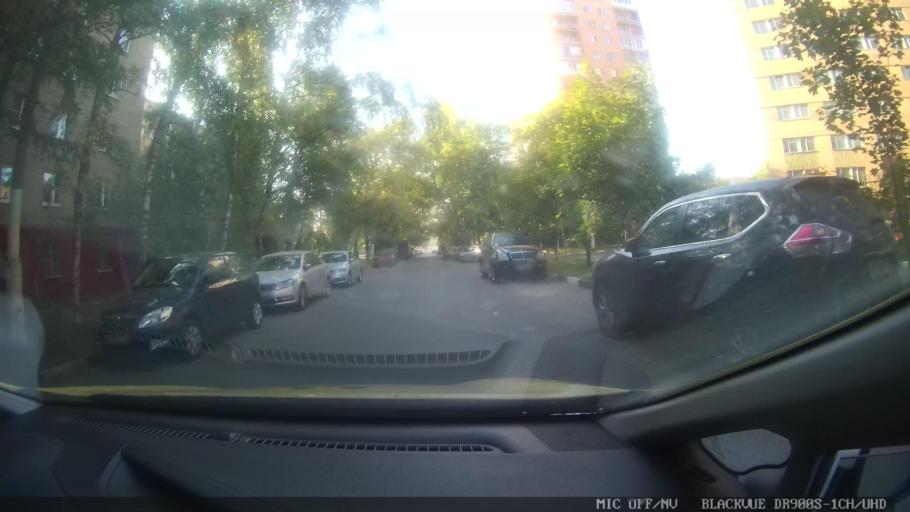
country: RU
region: Moskovskaya
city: Lyubertsy
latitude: 55.6777
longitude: 37.8749
